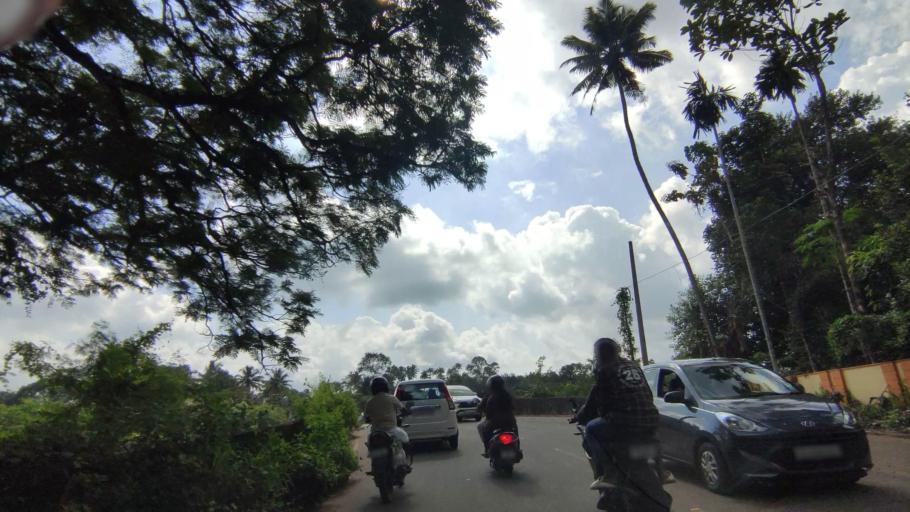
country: IN
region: Kerala
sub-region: Kottayam
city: Kottayam
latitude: 9.6757
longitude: 76.5450
